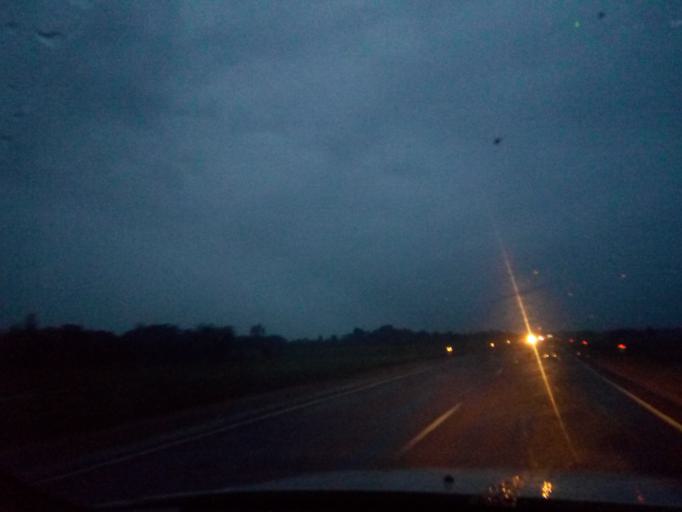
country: RU
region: Primorskiy
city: Dal'nerechensk
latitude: 45.9103
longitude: 133.7619
